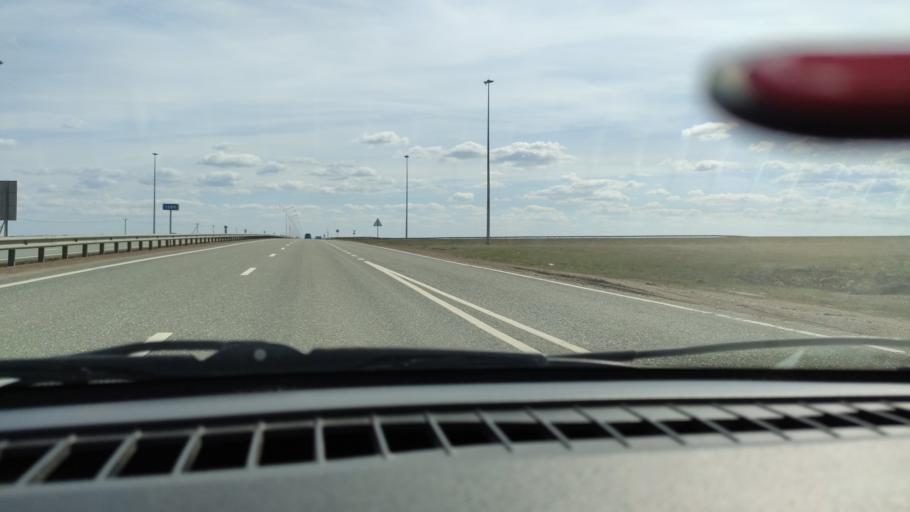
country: RU
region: Bashkortostan
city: Kushnarenkovo
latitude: 55.0744
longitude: 55.2838
